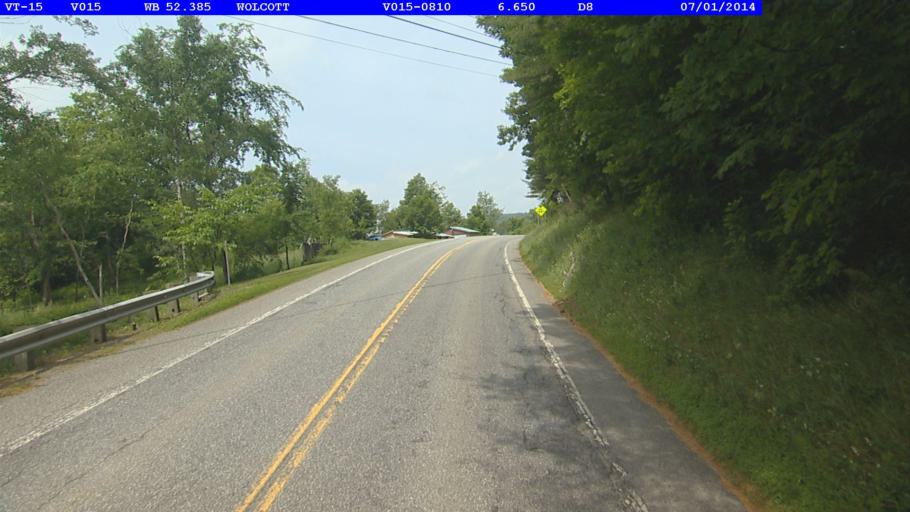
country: US
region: Vermont
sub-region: Caledonia County
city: Hardwick
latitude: 44.5293
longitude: -72.4233
